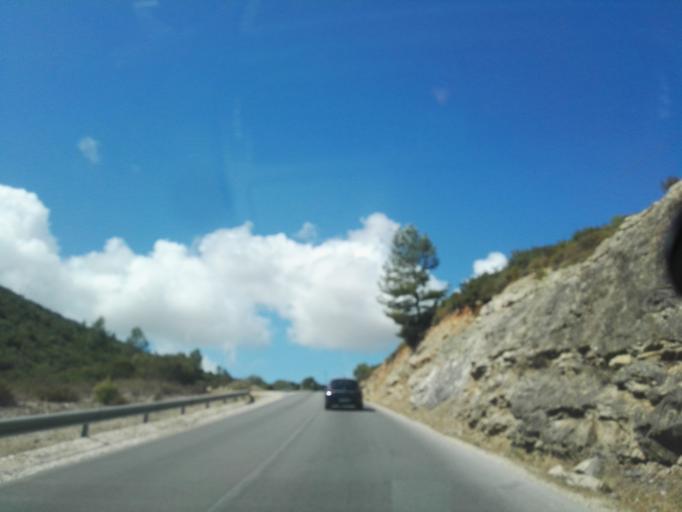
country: PT
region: Setubal
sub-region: Sesimbra
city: Sesimbra
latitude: 38.4430
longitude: -9.0856
